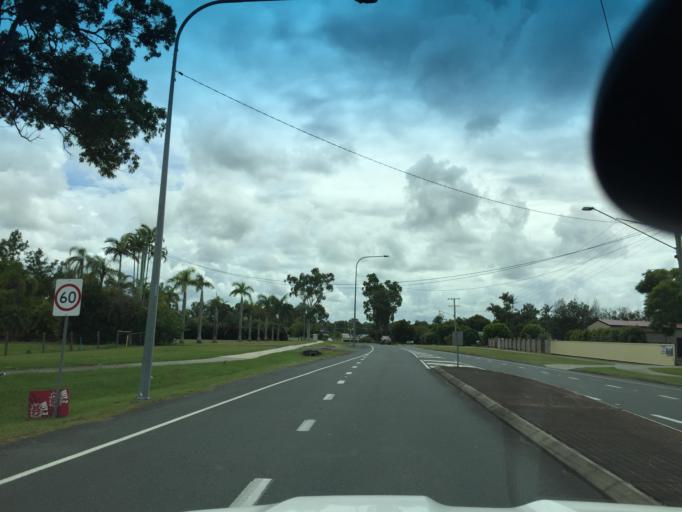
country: AU
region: Queensland
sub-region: Moreton Bay
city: Burpengary
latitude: -27.1381
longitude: 152.9825
